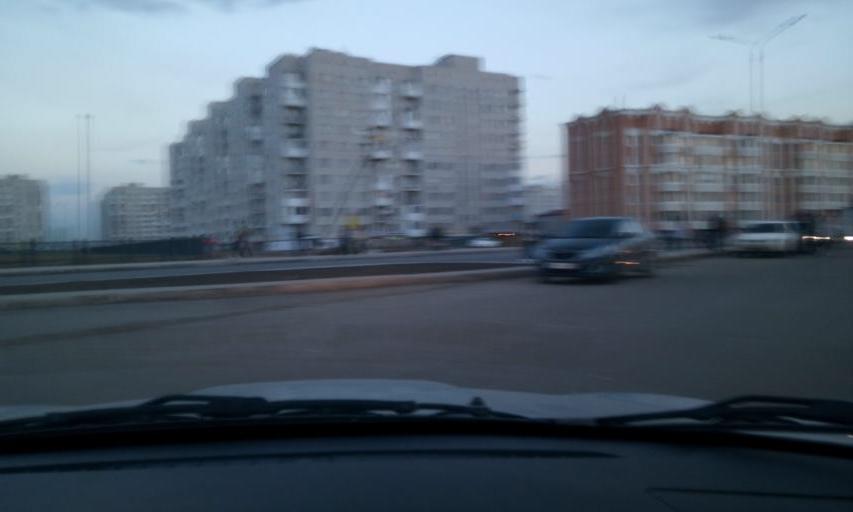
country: KZ
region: Astana Qalasy
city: Astana
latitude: 51.1246
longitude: 71.5003
